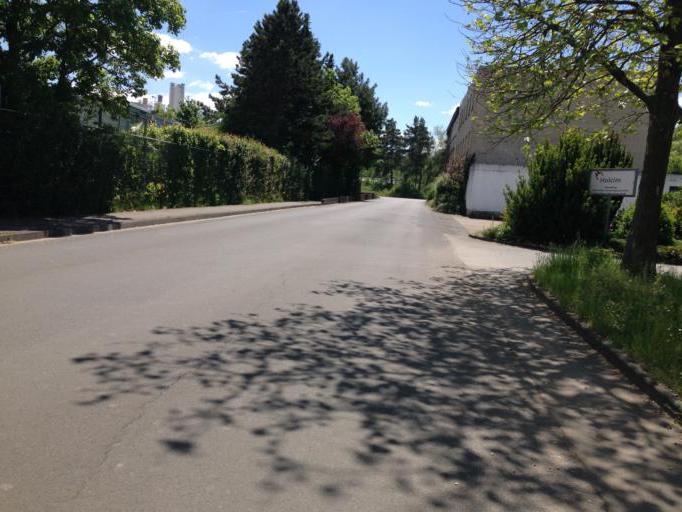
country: DE
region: Hesse
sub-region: Regierungsbezirk Giessen
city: Heuchelheim
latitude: 50.5768
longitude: 8.6348
